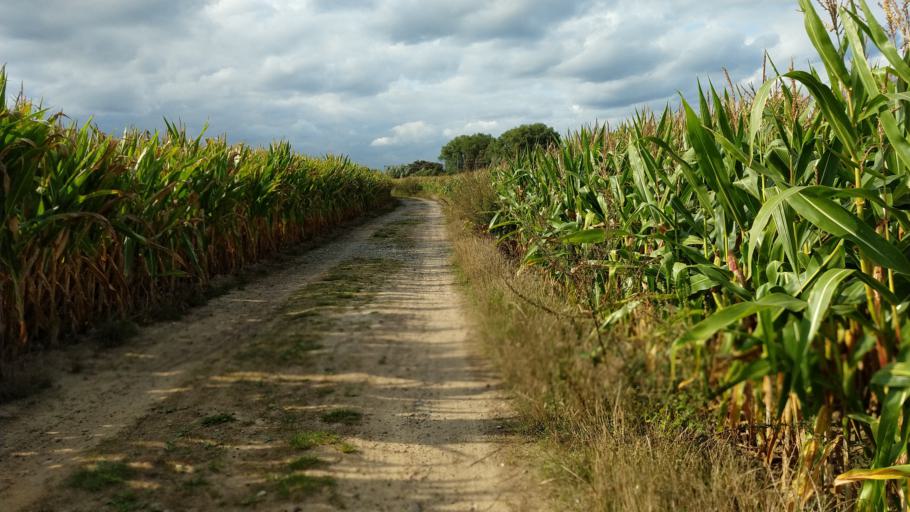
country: BE
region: Flanders
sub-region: Provincie Oost-Vlaanderen
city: Melle
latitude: 50.9921
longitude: 3.8156
